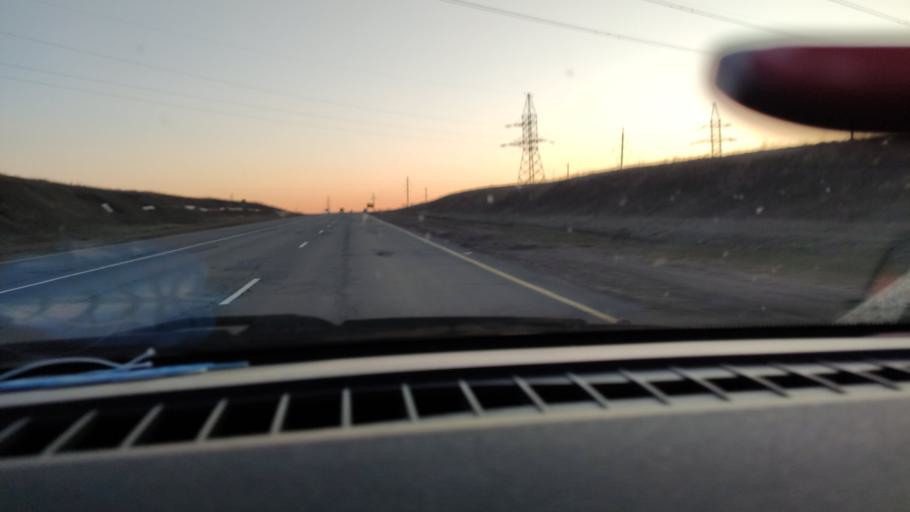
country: RU
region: Saratov
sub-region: Saratovskiy Rayon
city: Saratov
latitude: 51.7661
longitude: 46.0780
